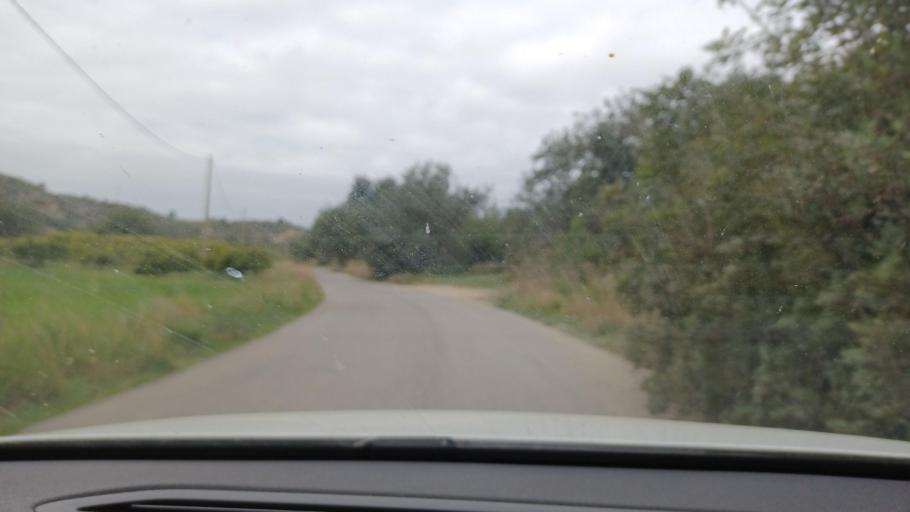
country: ES
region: Catalonia
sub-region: Provincia de Tarragona
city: Tortosa
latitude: 40.7897
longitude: 0.4928
